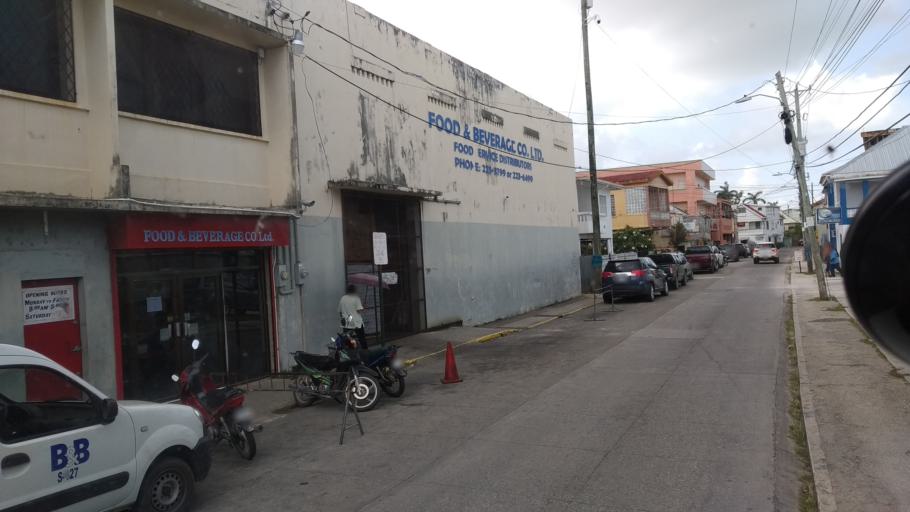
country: BZ
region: Belize
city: Belize City
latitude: 17.4988
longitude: -88.1877
